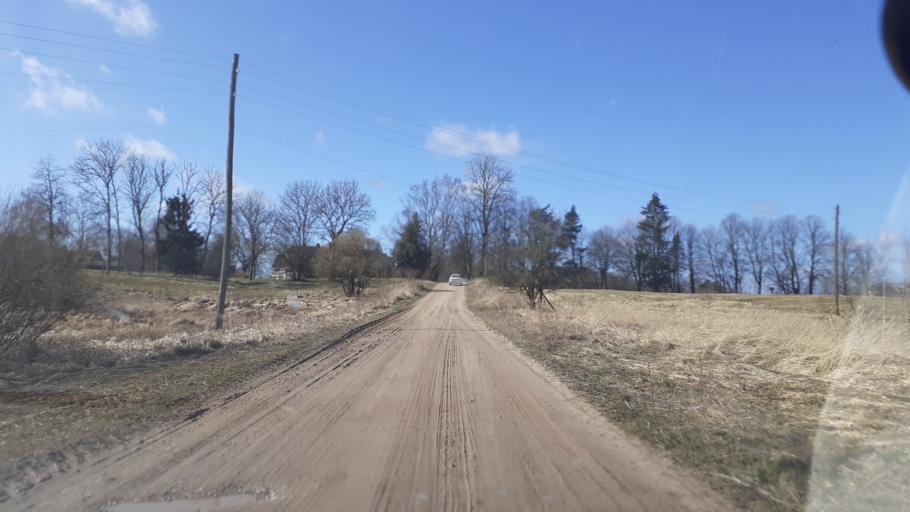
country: LV
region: Kuldigas Rajons
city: Kuldiga
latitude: 56.9337
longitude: 22.1593
